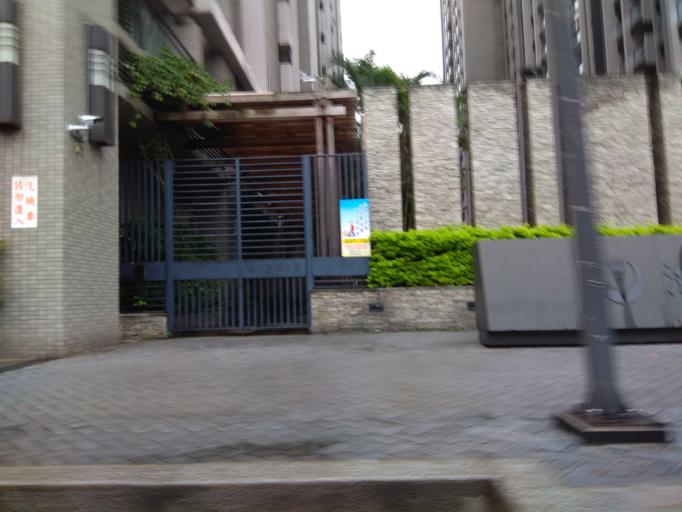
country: TW
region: Taiwan
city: Taoyuan City
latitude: 24.9656
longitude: 121.2234
